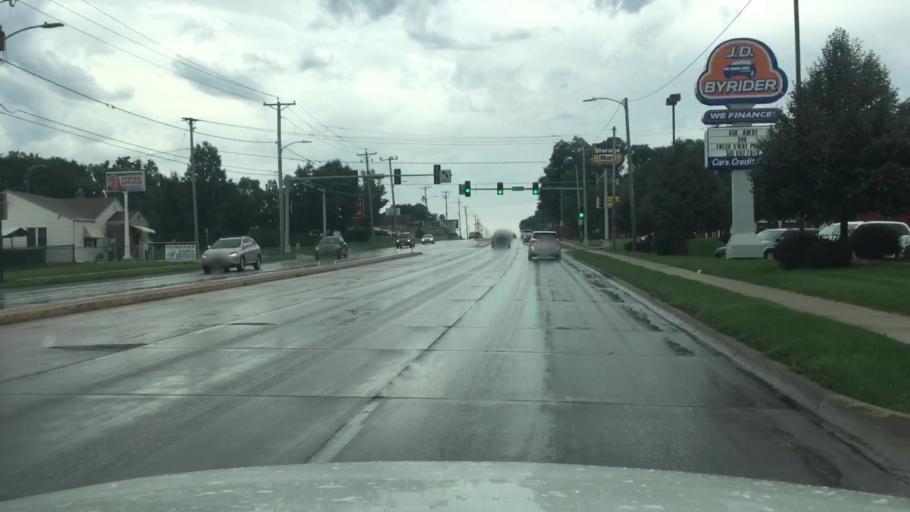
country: US
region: Iowa
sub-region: Polk County
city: Des Moines
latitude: 41.5632
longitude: -93.5971
